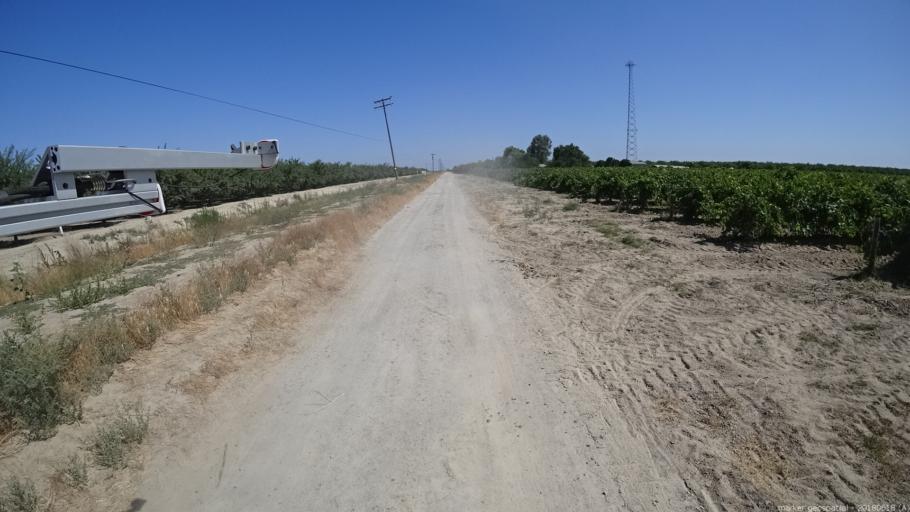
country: US
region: California
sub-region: Madera County
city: Parkwood
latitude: 36.8536
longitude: -120.2010
